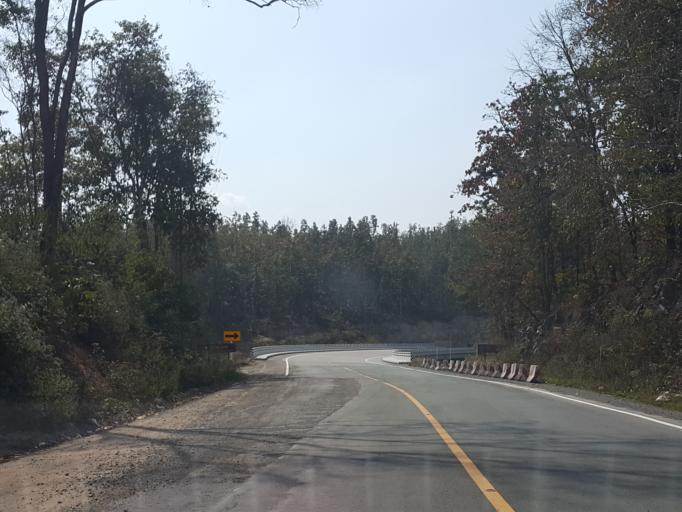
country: TH
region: Chiang Mai
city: Hot
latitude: 18.1769
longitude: 98.4515
